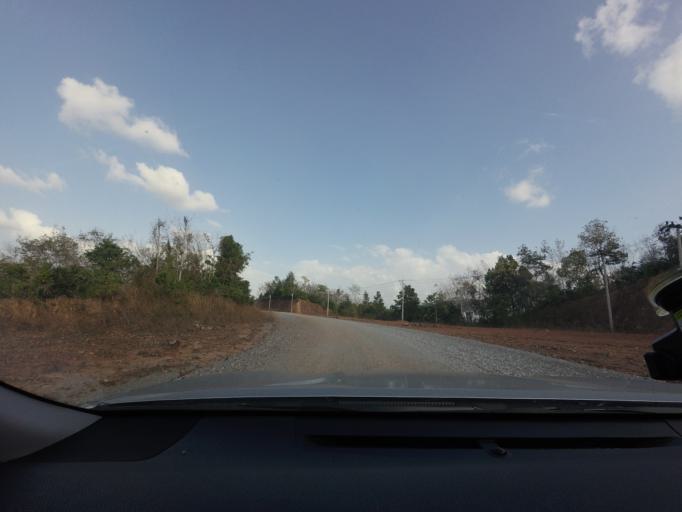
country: TH
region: Pattani
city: Mae Lan
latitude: 6.6057
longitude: 101.2439
